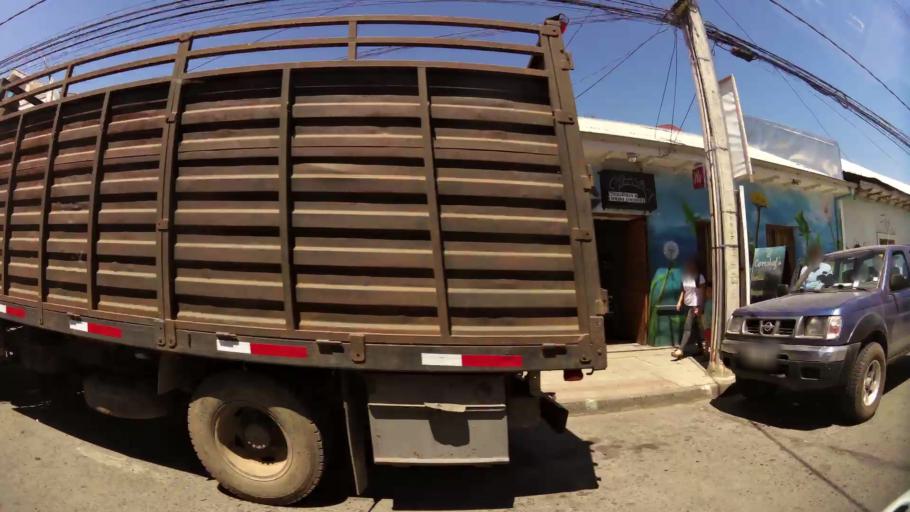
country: CL
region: Maule
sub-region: Provincia de Curico
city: Curico
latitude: -34.9853
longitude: -71.2320
